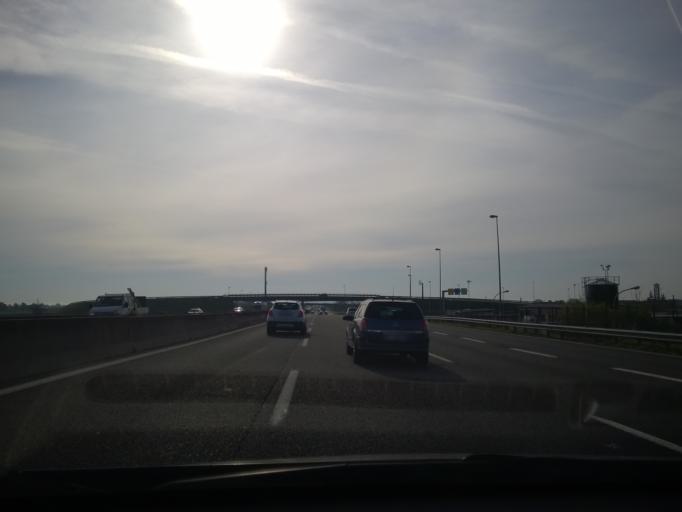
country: IT
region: Emilia-Romagna
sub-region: Provincia di Bologna
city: Imola
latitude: 44.3812
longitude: 11.7407
